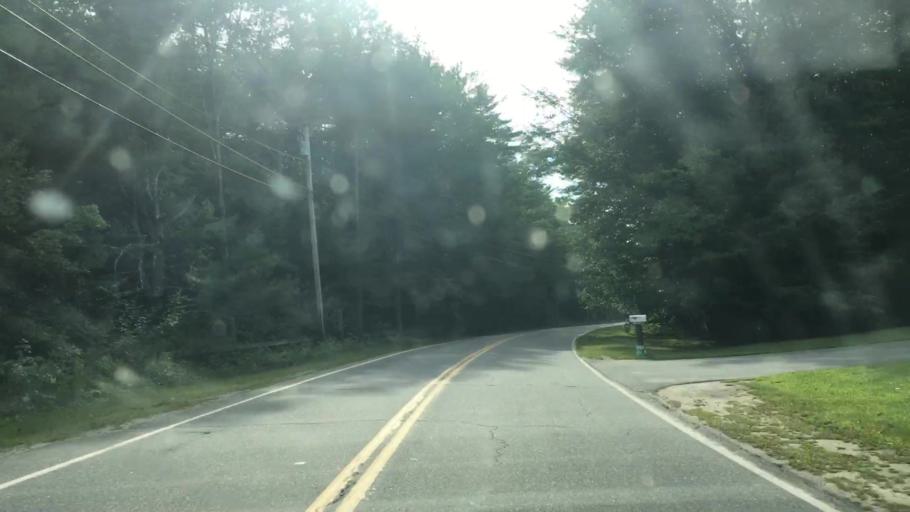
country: US
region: Maine
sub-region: Sagadahoc County
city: Bath
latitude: 43.9312
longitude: -69.8840
